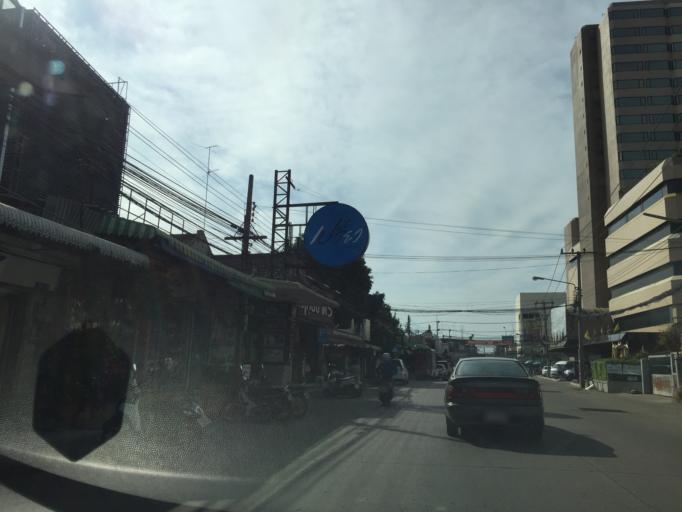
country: TH
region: Phitsanulok
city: Phitsanulok
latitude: 16.8227
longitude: 100.2651
